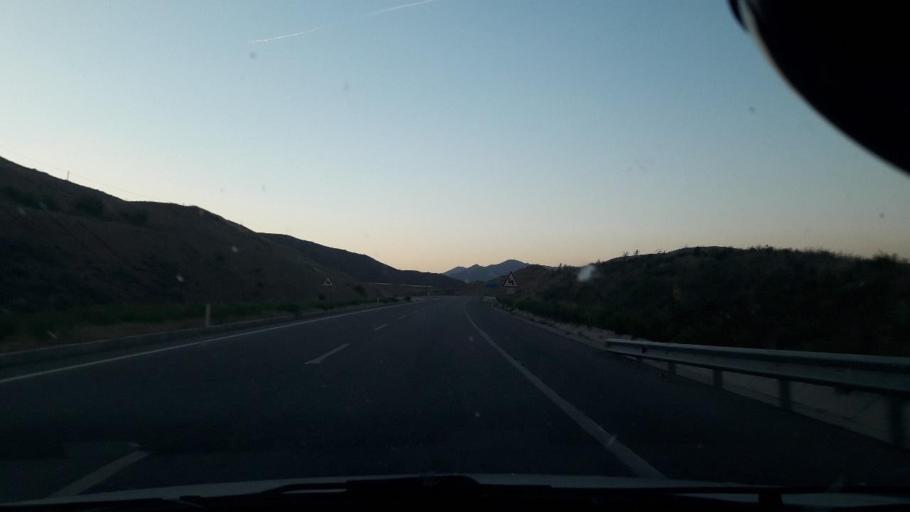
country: TR
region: Malatya
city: Yazihan
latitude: 38.6367
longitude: 38.1587
